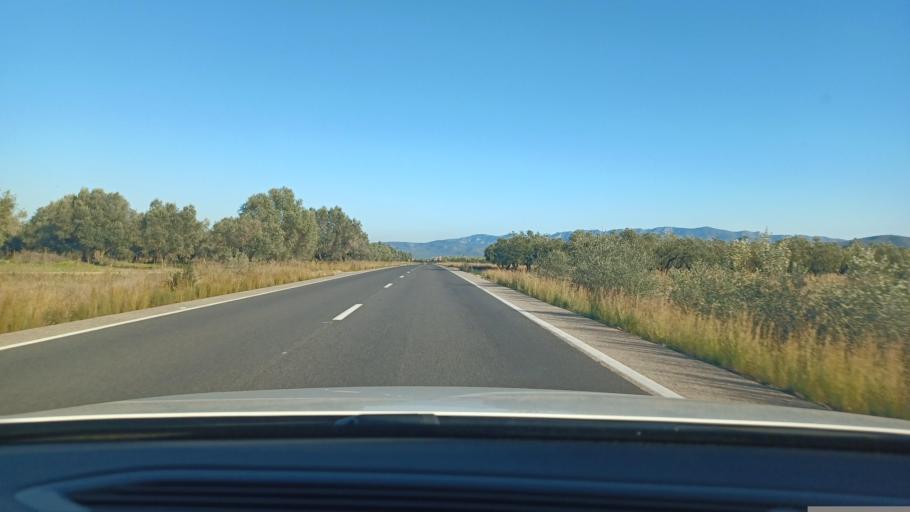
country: ES
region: Catalonia
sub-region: Provincia de Tarragona
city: Ulldecona
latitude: 40.6423
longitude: 0.3686
